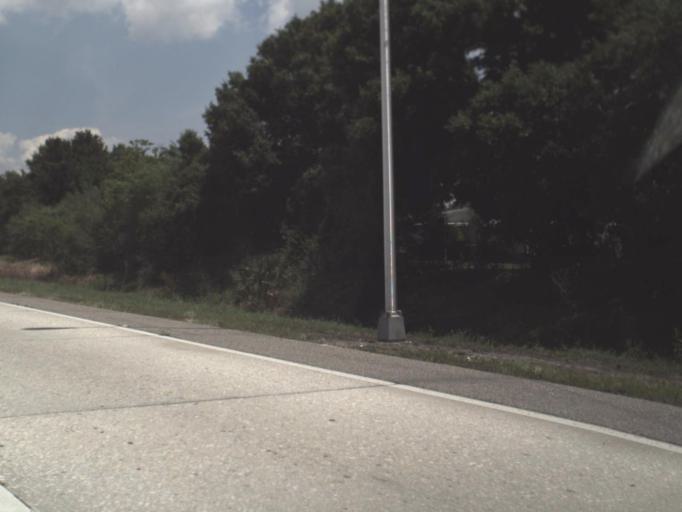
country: US
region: Florida
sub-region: Pinellas County
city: Lealman
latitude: 27.8474
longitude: -82.6635
